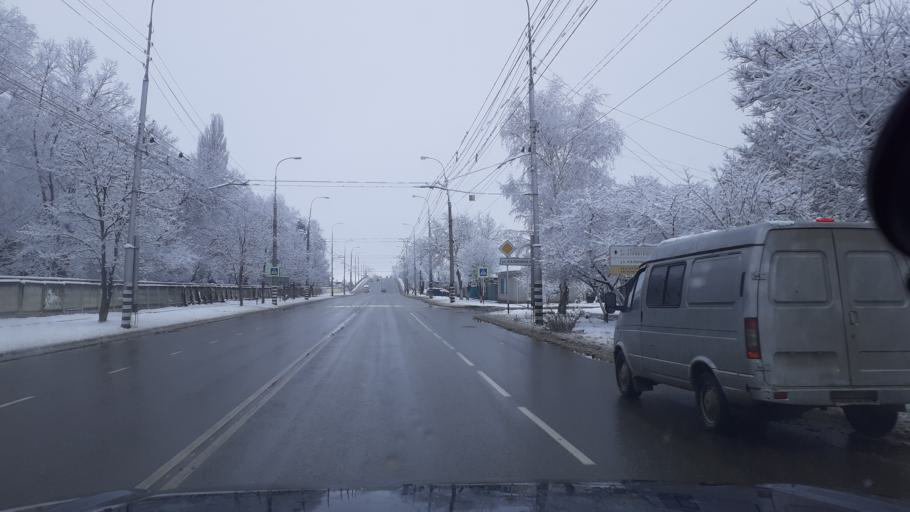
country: RU
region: Adygeya
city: Maykop
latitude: 44.6172
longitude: 40.1210
